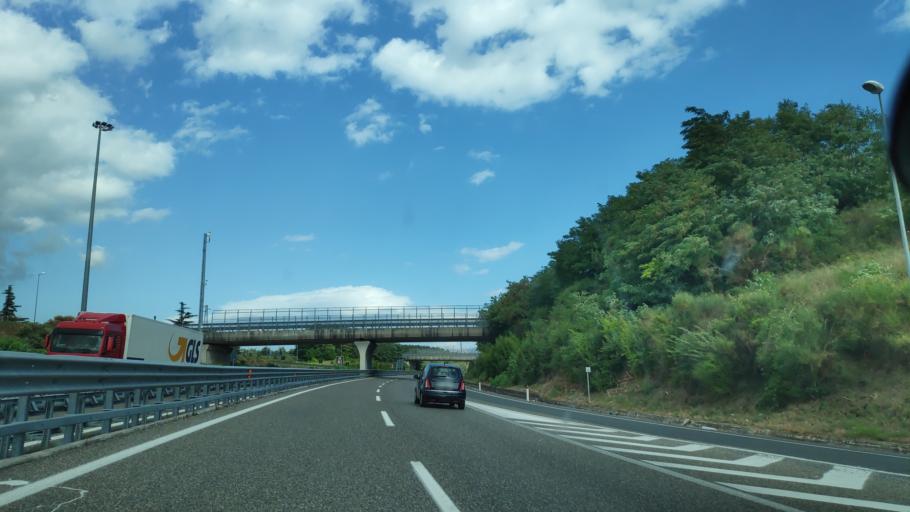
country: IT
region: Campania
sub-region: Provincia di Salerno
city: Palomonte
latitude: 40.6099
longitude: 15.2926
